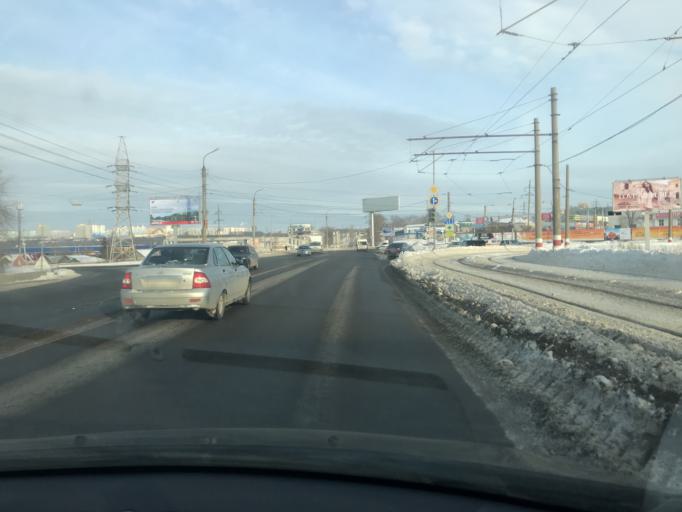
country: RU
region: Ulyanovsk
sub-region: Ulyanovskiy Rayon
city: Ulyanovsk
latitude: 54.3261
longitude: 48.3573
